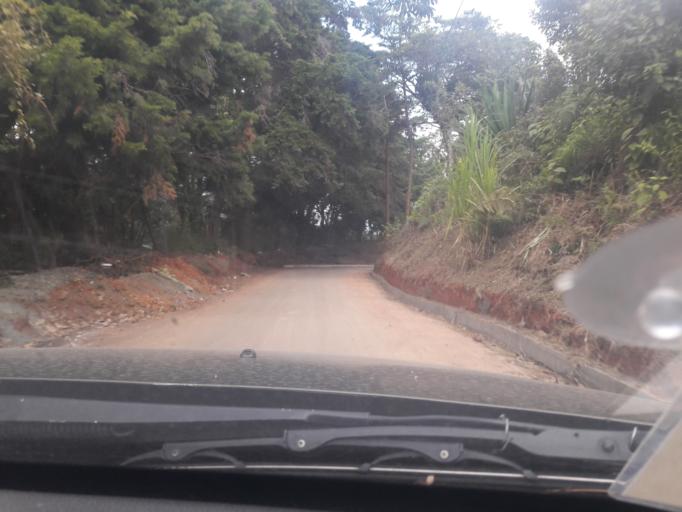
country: CO
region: Valle del Cauca
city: Cali
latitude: 3.4666
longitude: -76.6319
